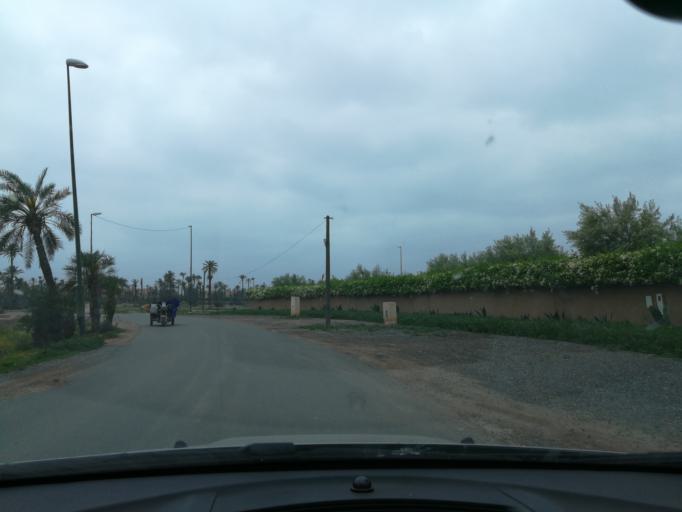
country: MA
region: Marrakech-Tensift-Al Haouz
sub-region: Marrakech
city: Marrakesh
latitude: 31.6786
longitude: -7.9857
